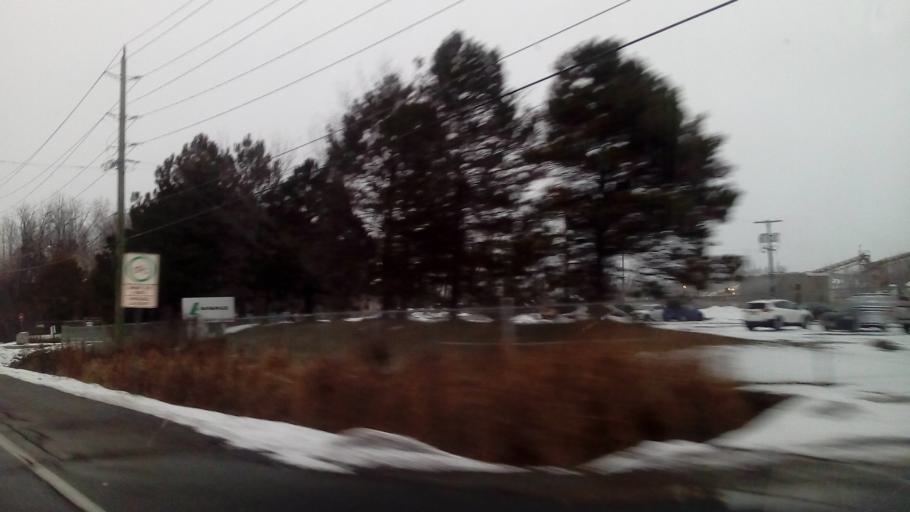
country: CA
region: Ontario
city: Ottawa
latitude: 45.4443
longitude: -75.5761
